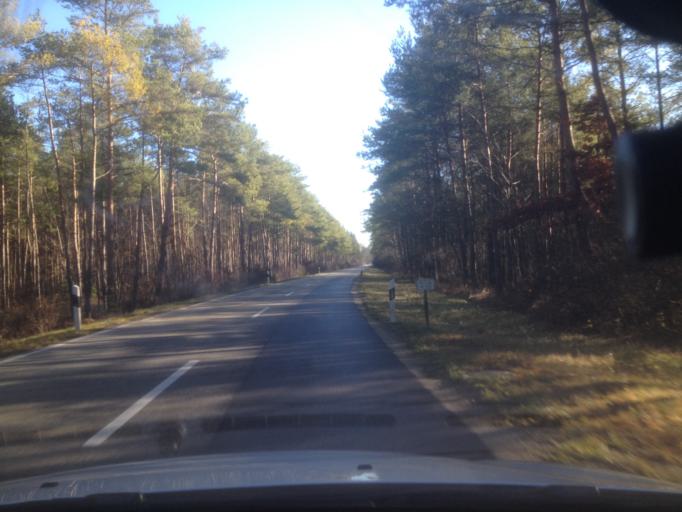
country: DE
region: Bavaria
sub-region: Upper Bavaria
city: Langenbach
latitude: 48.4157
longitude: 11.8928
